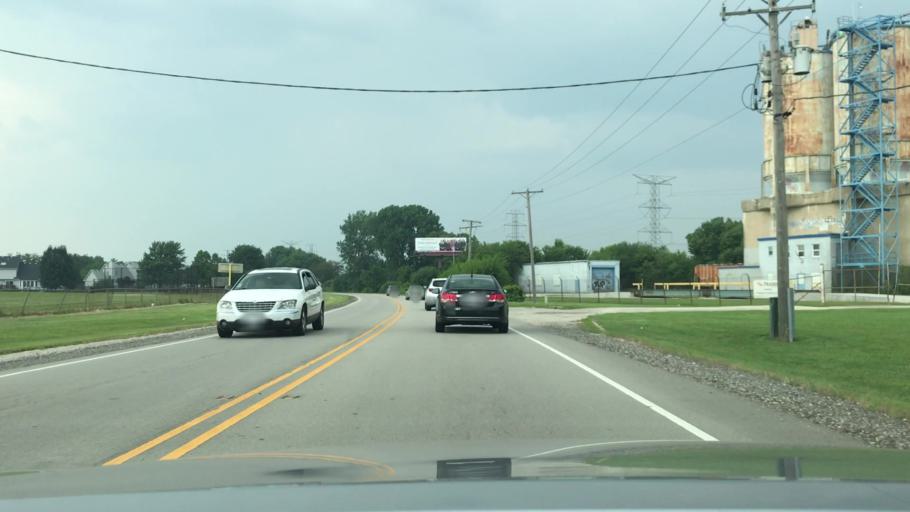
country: US
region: Illinois
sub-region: Will County
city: Plainfield
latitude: 41.6384
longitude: -88.2225
